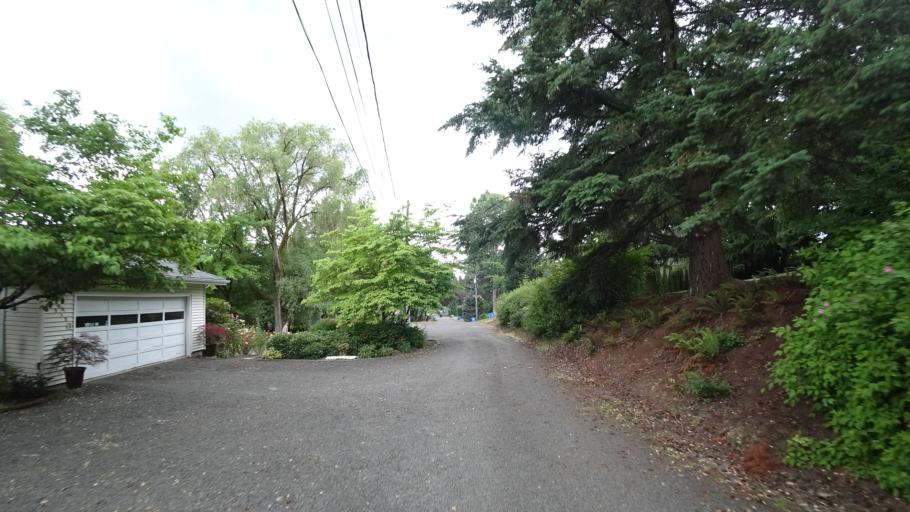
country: US
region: Oregon
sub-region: Clackamas County
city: Lake Oswego
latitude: 45.4605
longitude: -122.6940
